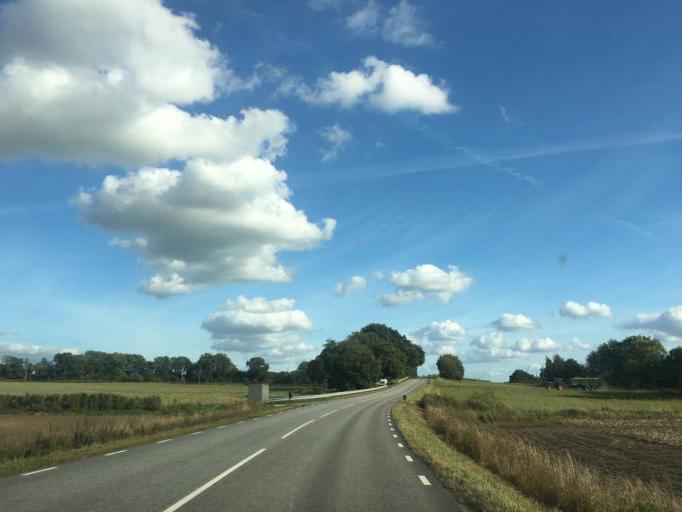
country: SE
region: Skane
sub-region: Hoors Kommun
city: Loberod
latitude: 55.7298
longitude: 13.4793
